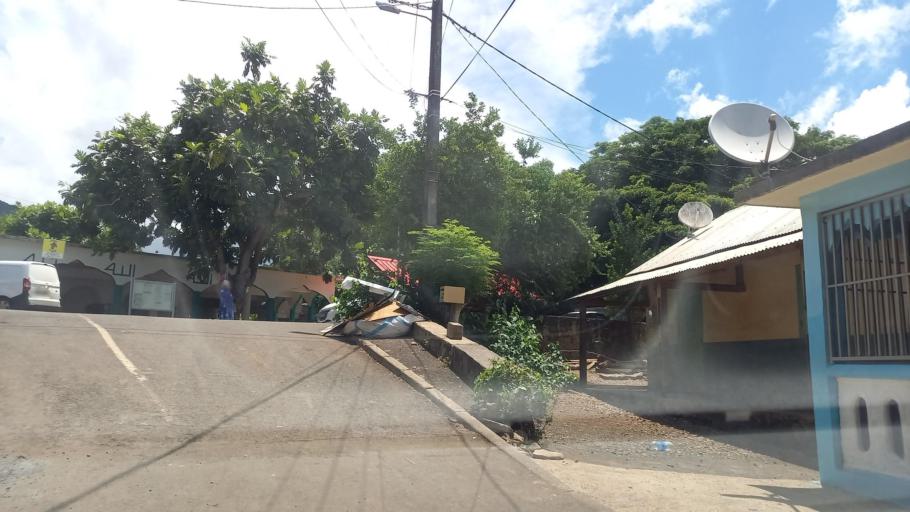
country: YT
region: Chirongui
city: Chirongui
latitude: -12.8933
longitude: 45.1413
